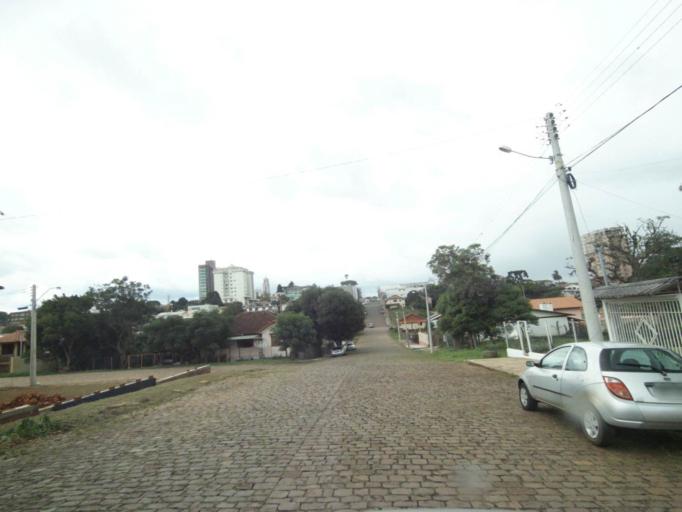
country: BR
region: Rio Grande do Sul
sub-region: Lagoa Vermelha
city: Lagoa Vermelha
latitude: -28.2059
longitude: -51.5266
